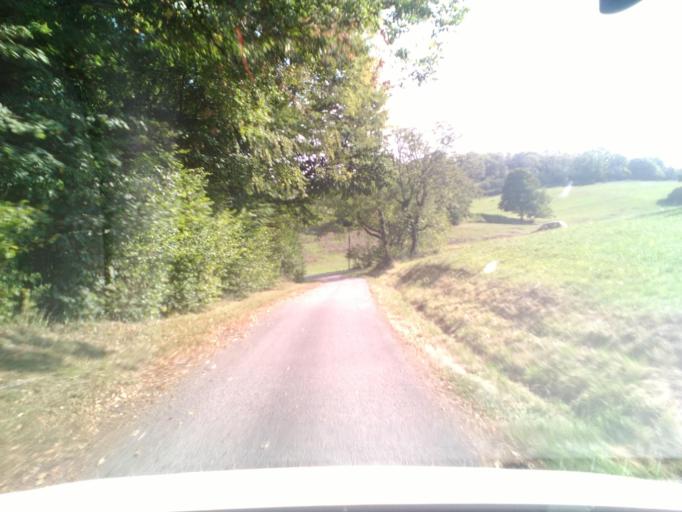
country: FR
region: Lorraine
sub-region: Departement des Vosges
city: Senones
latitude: 48.3502
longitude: 7.0079
